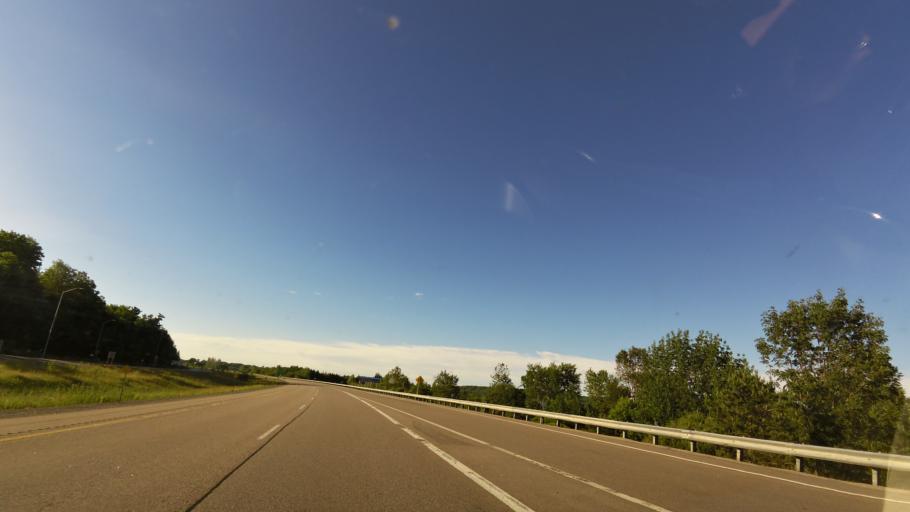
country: CA
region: Ontario
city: Orillia
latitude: 44.6644
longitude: -79.6426
